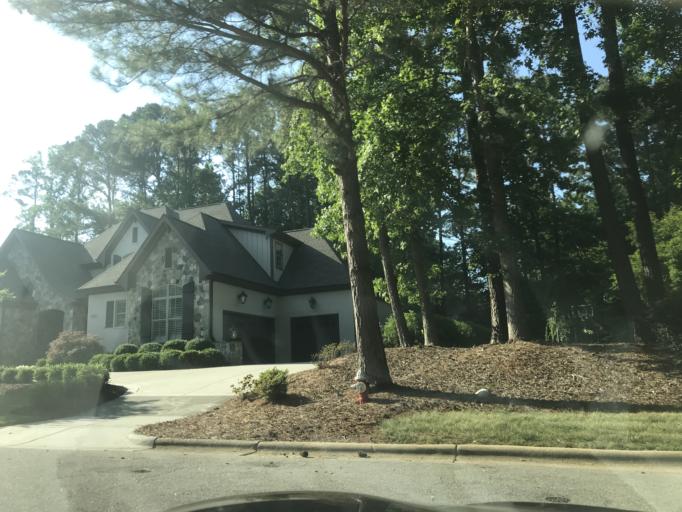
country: US
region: North Carolina
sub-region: Wake County
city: West Raleigh
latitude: 35.8821
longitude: -78.6013
